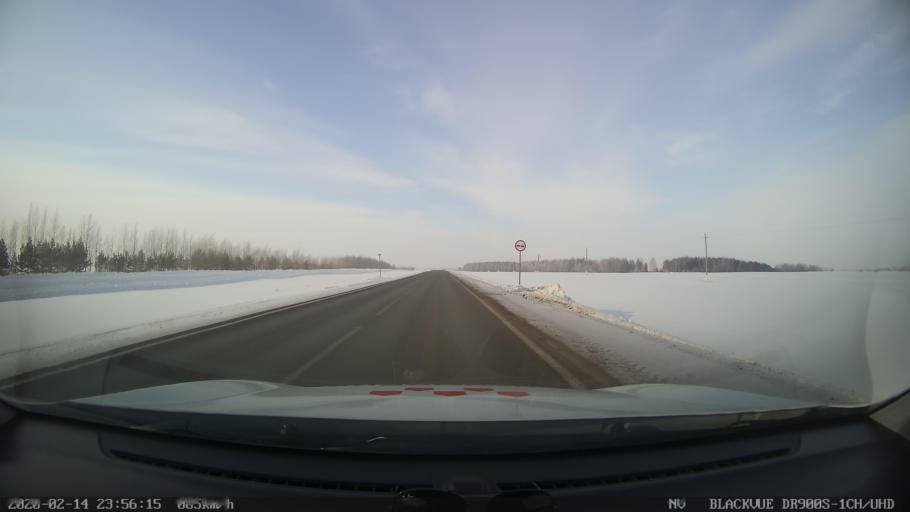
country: RU
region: Tatarstan
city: Kuybyshevskiy Zaton
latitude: 55.3230
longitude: 49.1329
